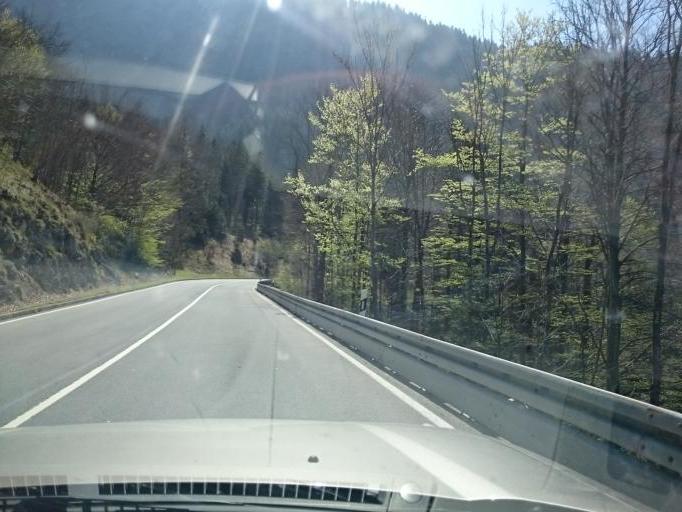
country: DE
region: Bavaria
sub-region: Upper Bavaria
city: Kochel
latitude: 47.6287
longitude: 11.3546
